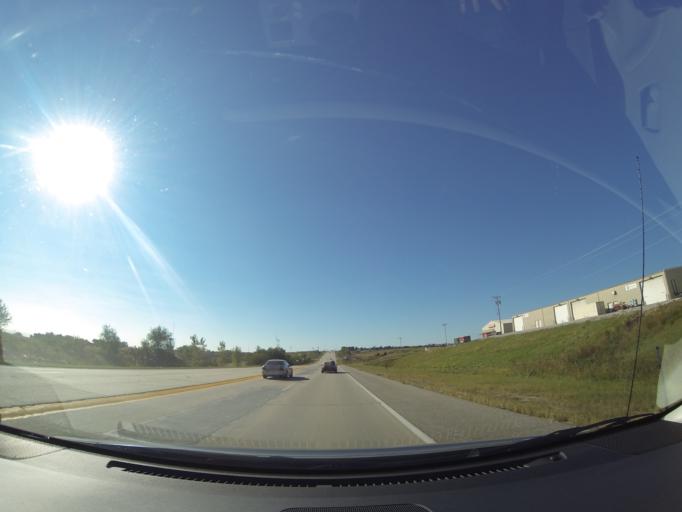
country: US
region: Nebraska
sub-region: Sarpy County
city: Gretna
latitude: 41.1078
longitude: -96.2534
